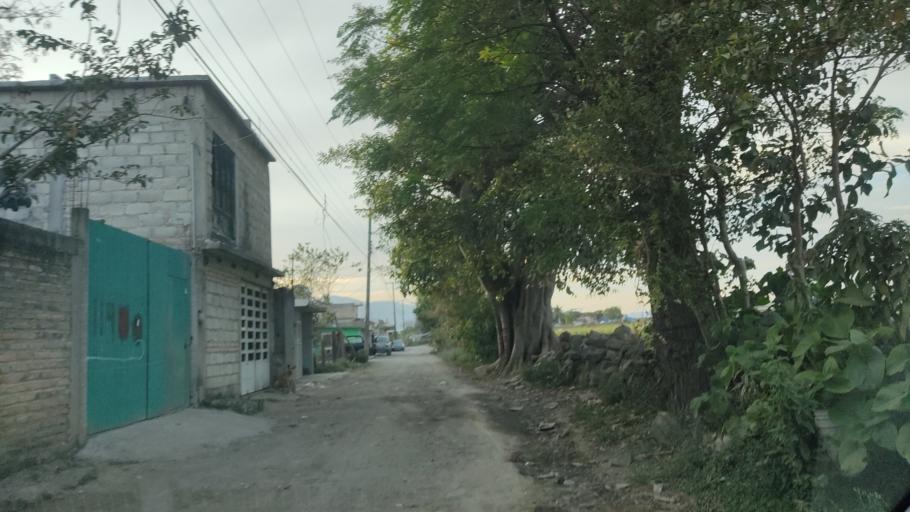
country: MX
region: Nayarit
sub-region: Tepic
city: La Corregidora
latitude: 21.4606
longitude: -104.8247
